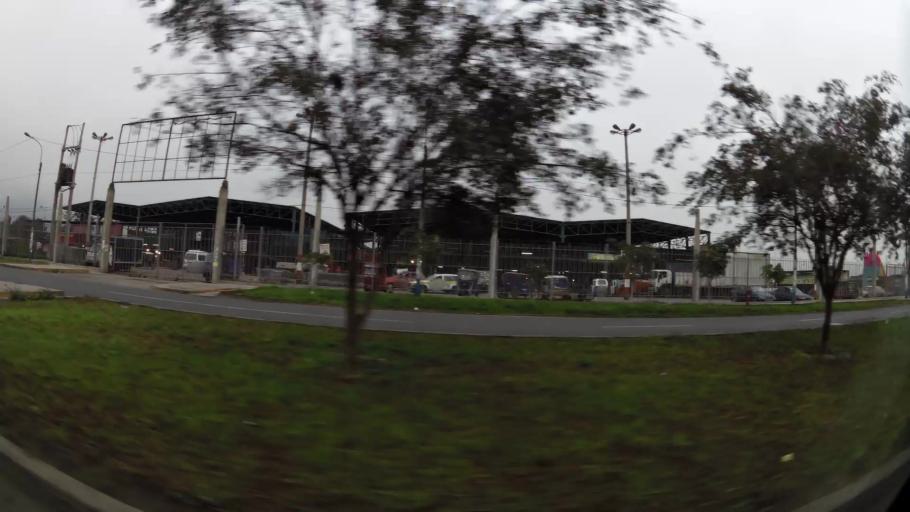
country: PE
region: Lima
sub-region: Lima
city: Independencia
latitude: -11.9376
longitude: -77.0662
